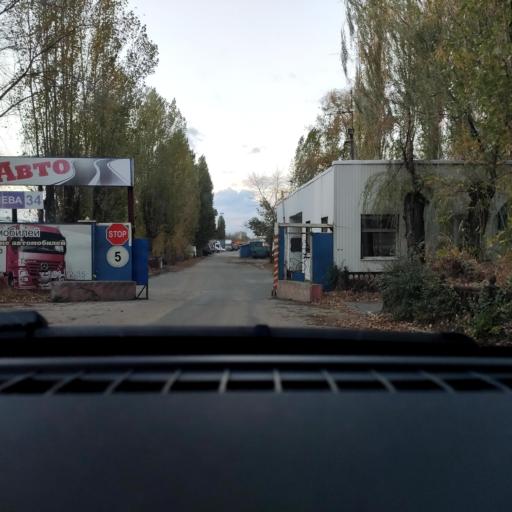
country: RU
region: Voronezj
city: Maslovka
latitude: 51.6018
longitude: 39.2620
